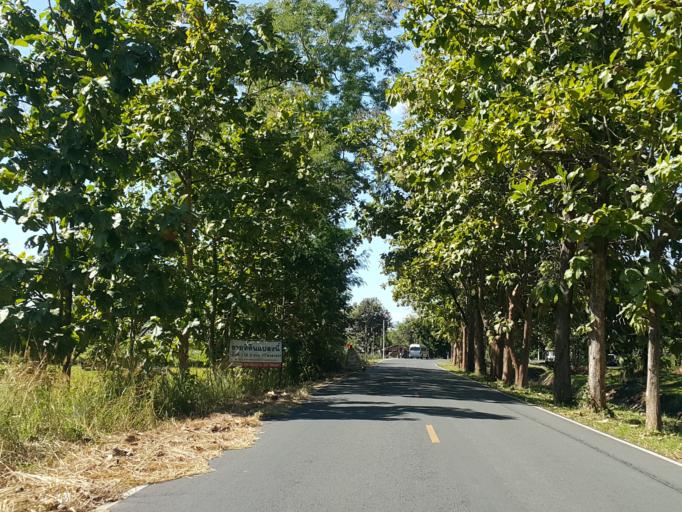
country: TH
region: Chiang Mai
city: San Sai
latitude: 18.8973
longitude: 99.1394
